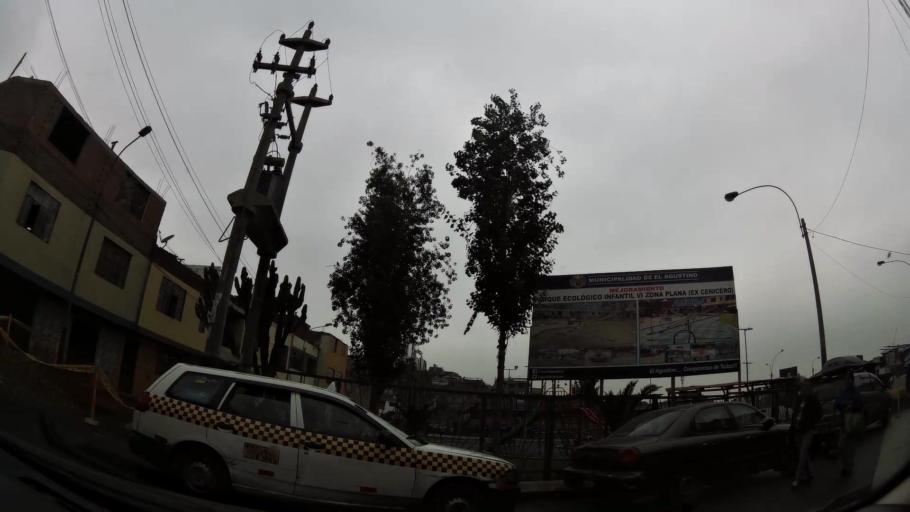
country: PE
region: Lima
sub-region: Lima
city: San Luis
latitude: -12.0543
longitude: -77.0024
